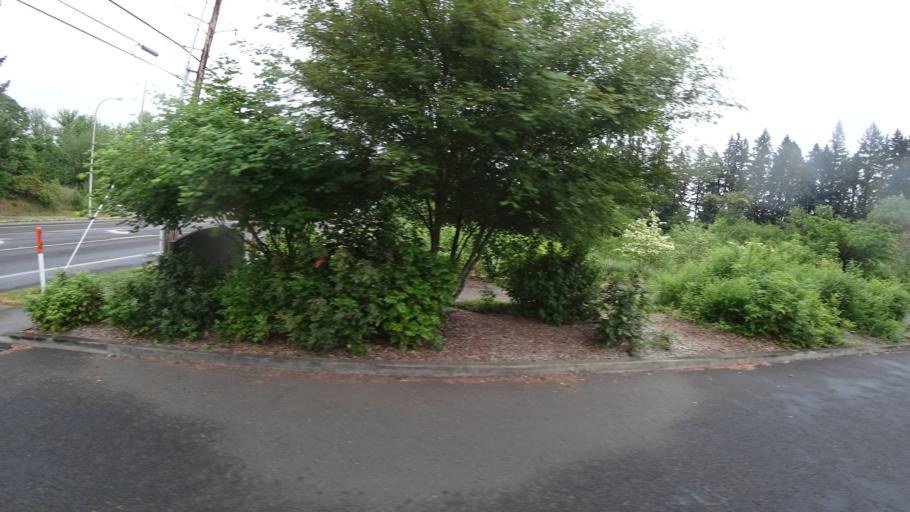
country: US
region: Oregon
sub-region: Washington County
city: Rockcreek
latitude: 45.5367
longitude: -122.8920
